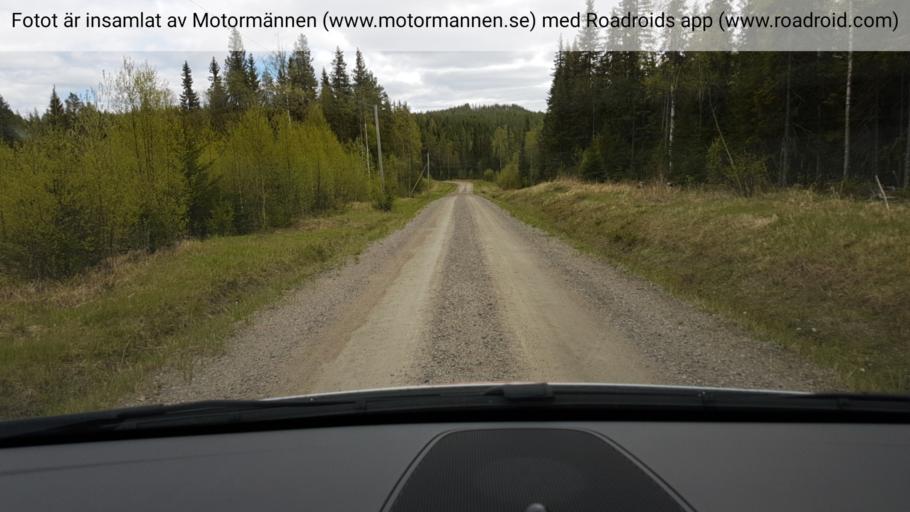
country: SE
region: Jaemtland
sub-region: Braecke Kommun
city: Braecke
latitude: 62.8023
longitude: 15.1161
